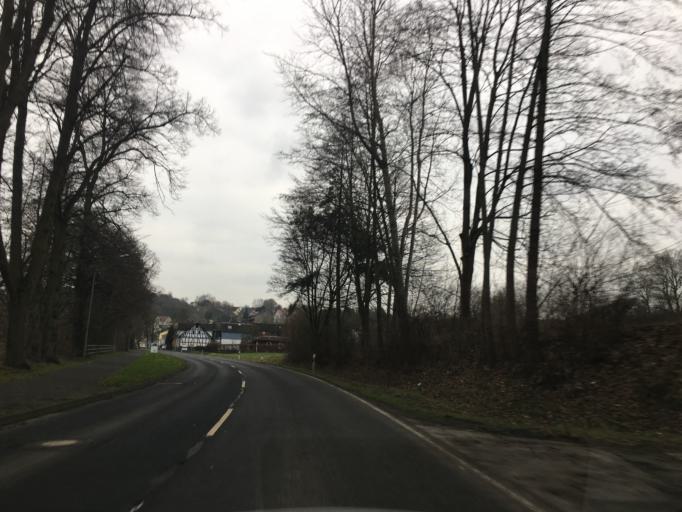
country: DE
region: Hesse
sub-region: Regierungsbezirk Giessen
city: Alsfeld
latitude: 50.7394
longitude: 9.2719
